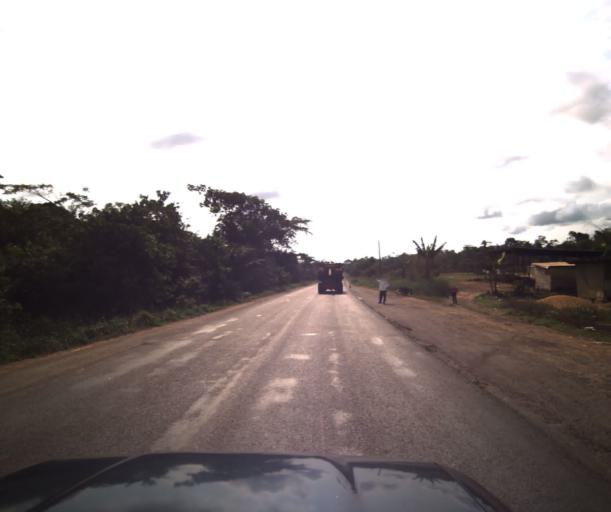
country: CM
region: Littoral
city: Edea
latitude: 3.9499
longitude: 10.0317
